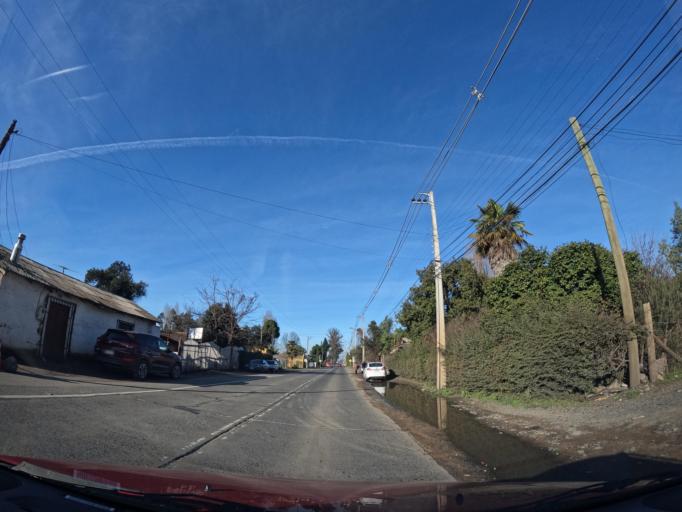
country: CL
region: Maule
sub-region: Provincia de Linares
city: San Javier
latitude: -35.5720
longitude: -71.6863
